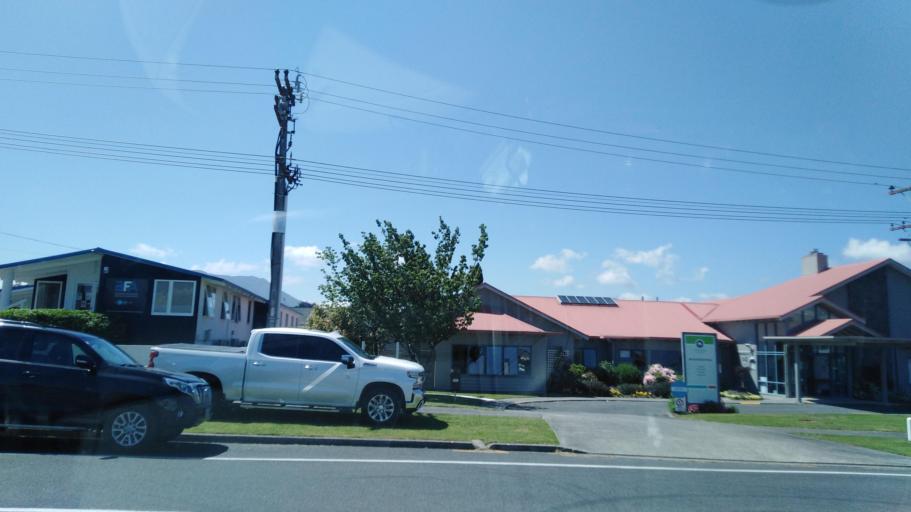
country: NZ
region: Waikato
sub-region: Taupo District
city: Taupo
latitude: -38.6902
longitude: 176.0767
